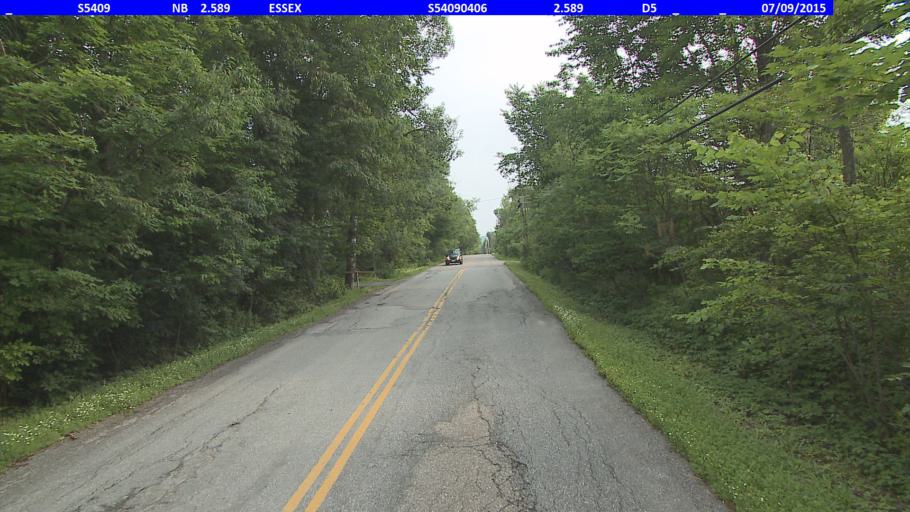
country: US
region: Vermont
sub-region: Chittenden County
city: Essex Junction
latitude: 44.5459
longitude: -73.0715
